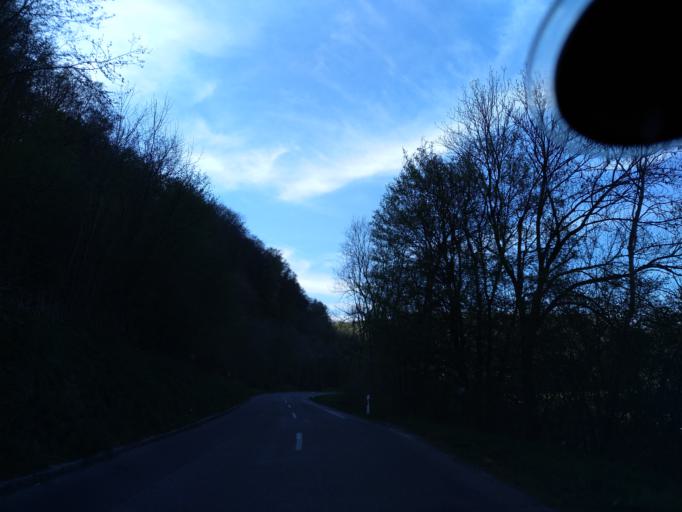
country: DE
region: Baden-Wuerttemberg
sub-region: Regierungsbezirk Stuttgart
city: Langenburg
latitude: 49.2309
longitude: 9.9057
